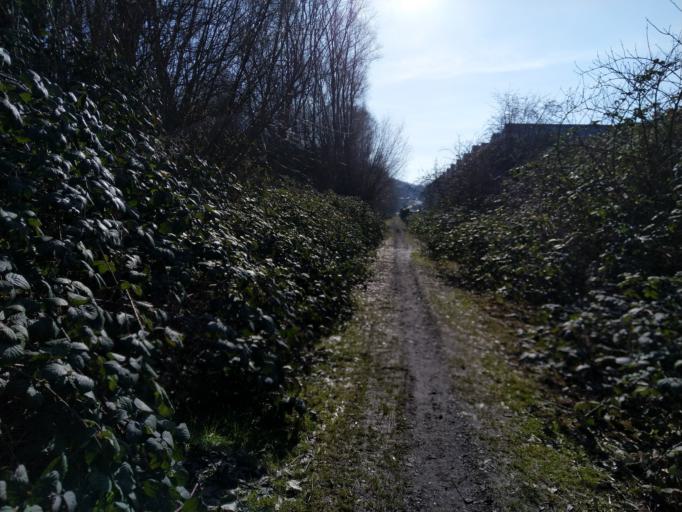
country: BE
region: Wallonia
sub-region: Province du Hainaut
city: Mons
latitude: 50.4442
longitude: 3.9375
